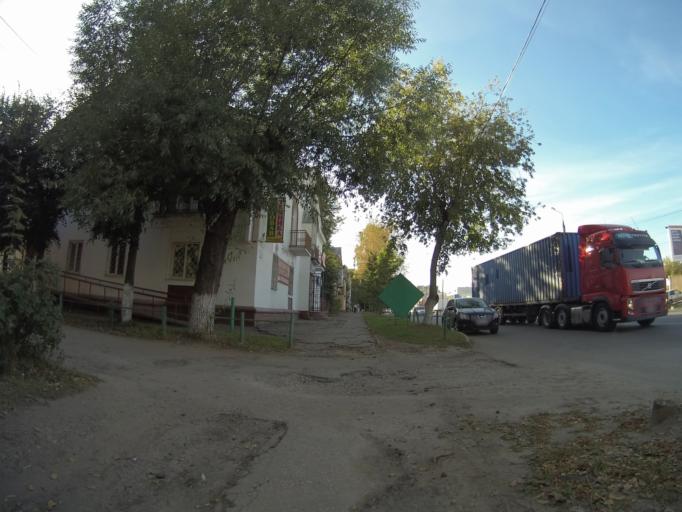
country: RU
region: Vladimir
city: Vladimir
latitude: 56.1494
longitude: 40.3821
